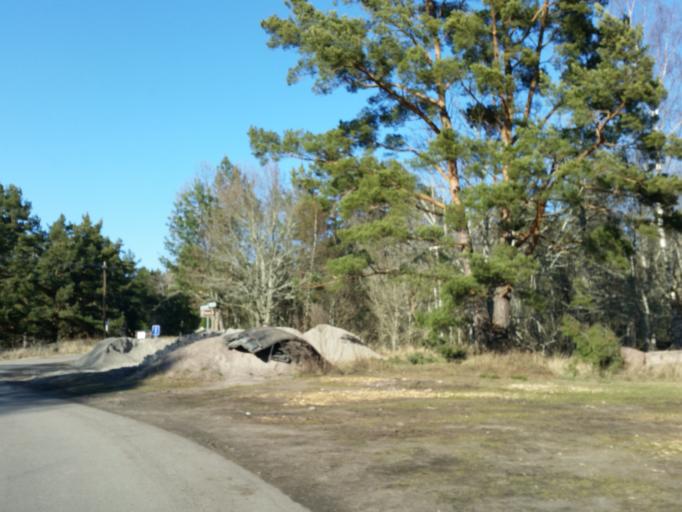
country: SE
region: Kalmar
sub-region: Oskarshamns Kommun
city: Paskallavik
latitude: 57.1864
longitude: 16.4521
